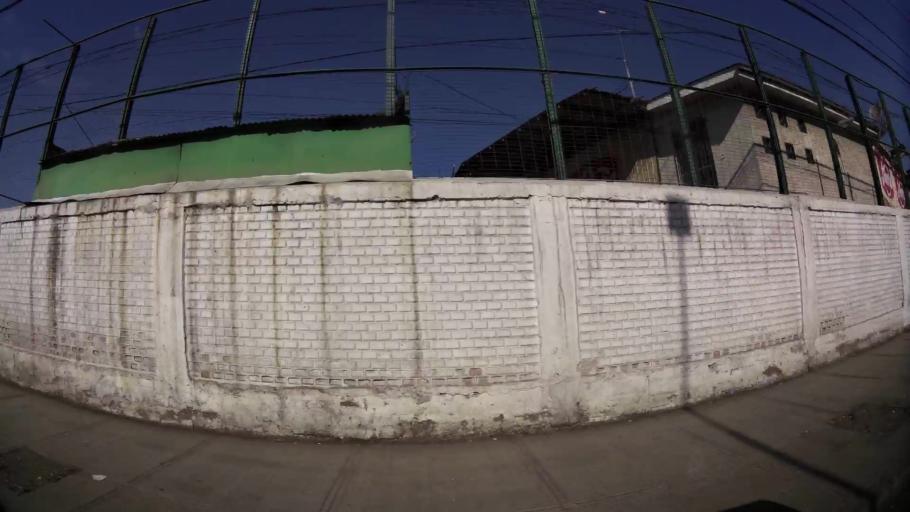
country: CL
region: Santiago Metropolitan
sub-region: Provincia de Santiago
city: Santiago
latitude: -33.4819
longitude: -70.6858
